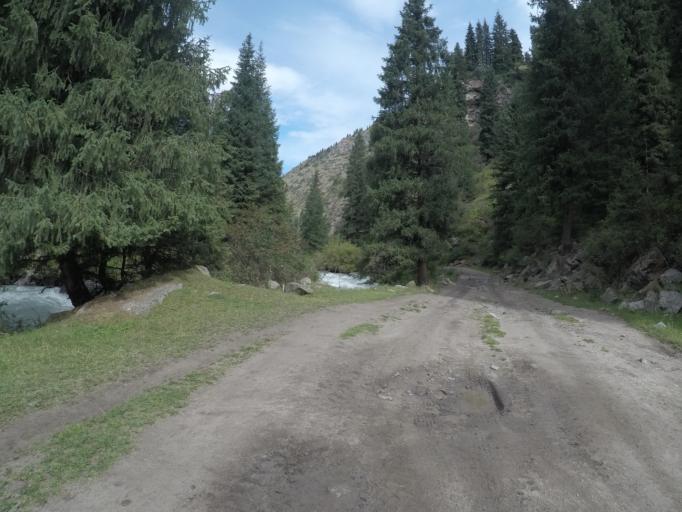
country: KG
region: Ysyk-Koel
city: Teploklyuchenka
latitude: 42.4377
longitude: 78.5600
